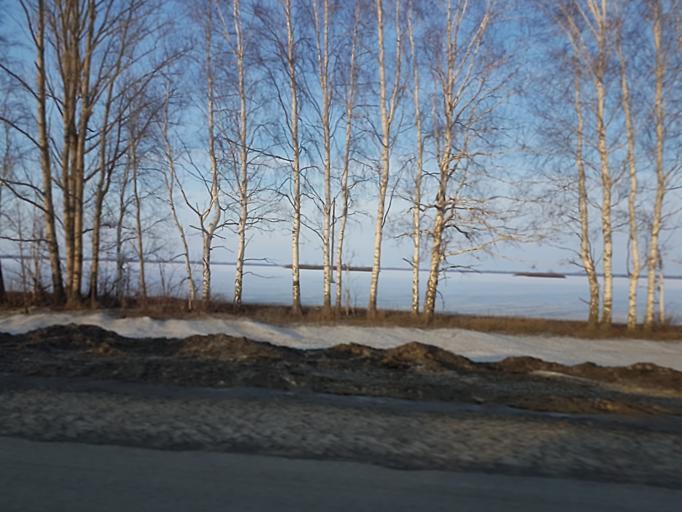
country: RU
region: Tambov
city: Selezni
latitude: 52.8212
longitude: 40.9244
